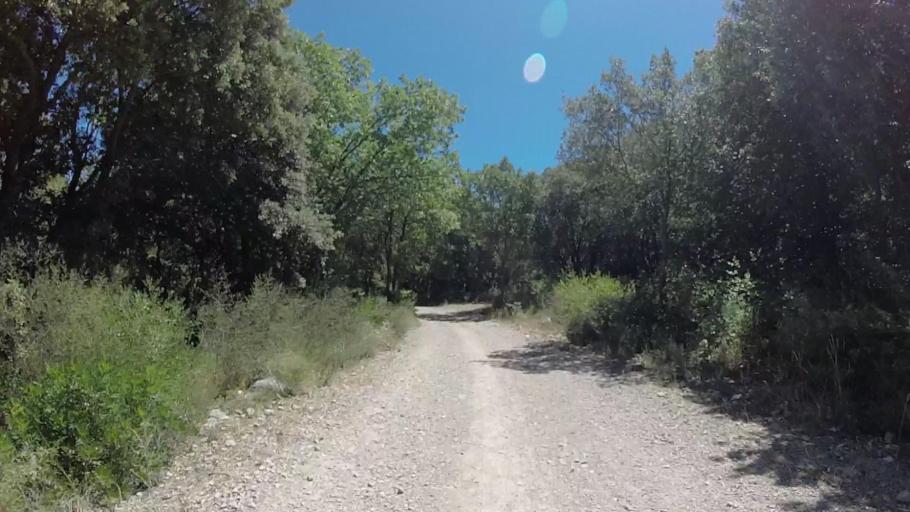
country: FR
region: Provence-Alpes-Cote d'Azur
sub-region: Departement des Alpes-Maritimes
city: Biot
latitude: 43.6300
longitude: 7.0501
